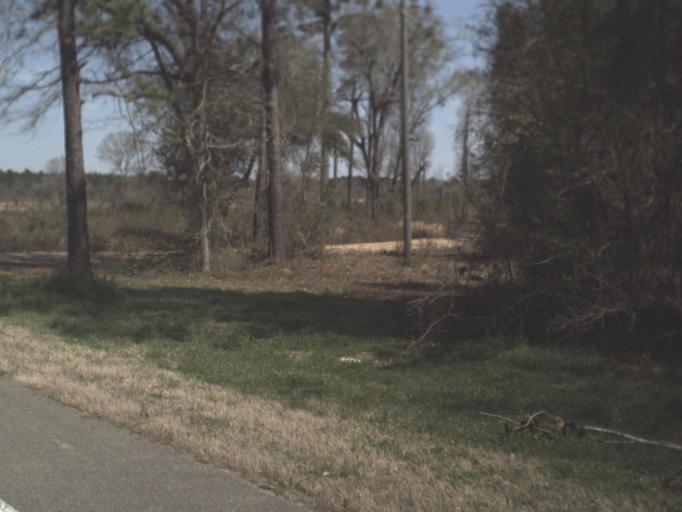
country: US
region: Florida
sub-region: Gadsden County
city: Gretna
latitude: 30.5845
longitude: -84.6948
